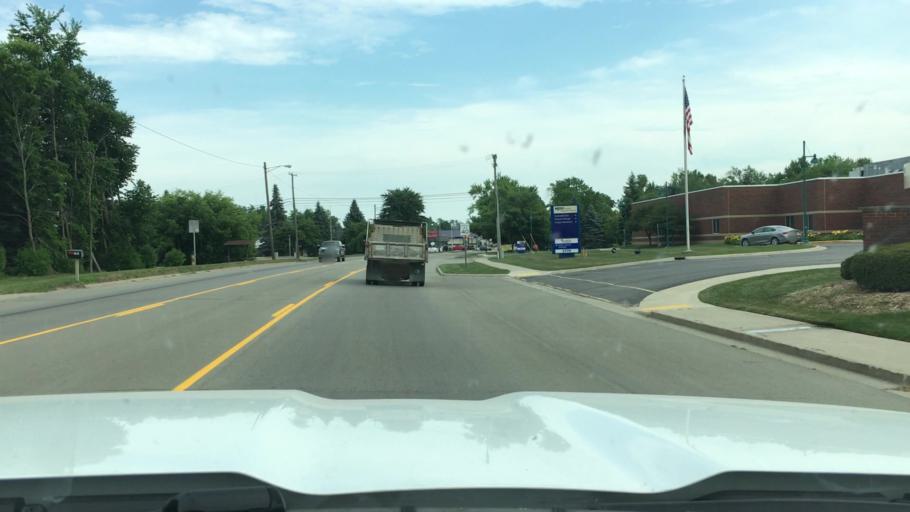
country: US
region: Michigan
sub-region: Sanilac County
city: Marlette
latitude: 43.3330
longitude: -83.0804
